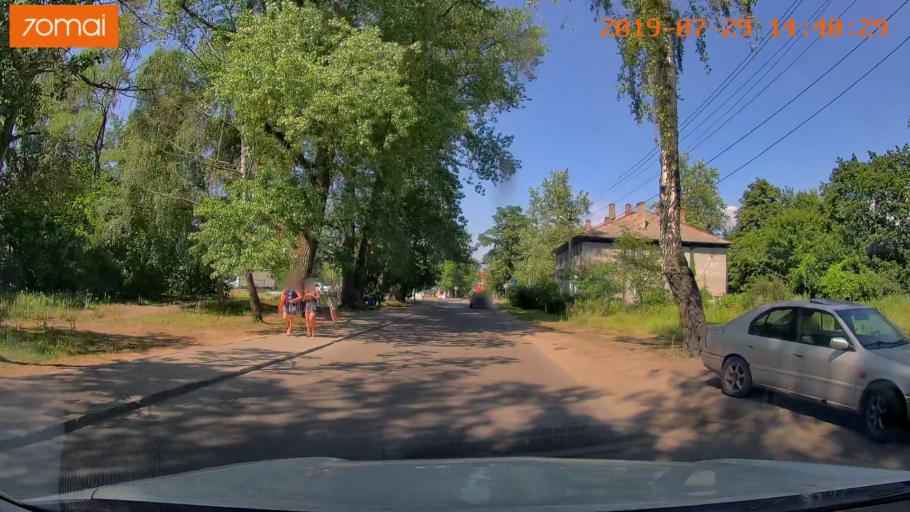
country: RU
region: Kaliningrad
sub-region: Gorod Kaliningrad
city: Baltiysk
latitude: 54.6545
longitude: 19.9012
